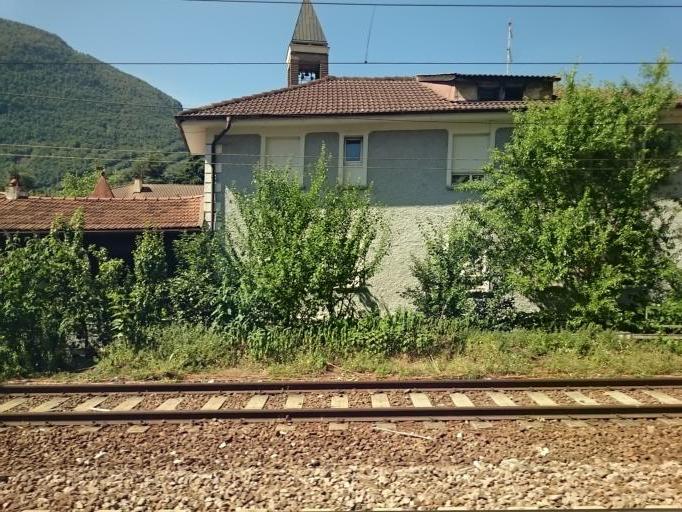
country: IT
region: Trentino-Alto Adige
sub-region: Bolzano
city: Cardano
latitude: 46.4986
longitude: 11.3693
